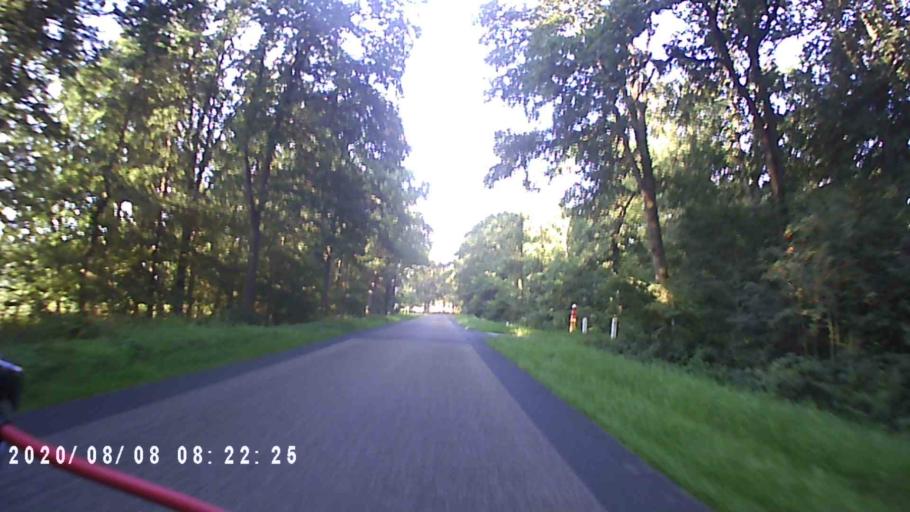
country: NL
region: Groningen
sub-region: Gemeente Leek
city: Leek
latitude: 53.0903
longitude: 6.3121
